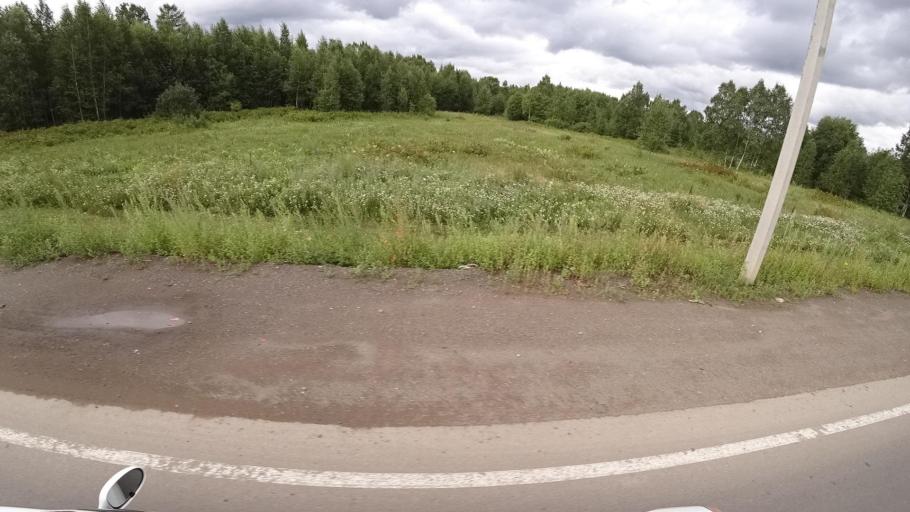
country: RU
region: Khabarovsk Krai
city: Solnechnyy
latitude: 50.5880
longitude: 137.0284
